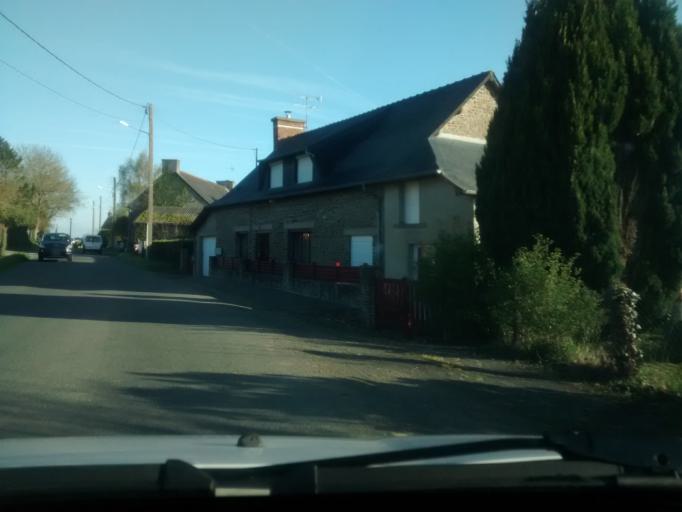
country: FR
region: Brittany
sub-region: Departement d'Ille-et-Vilaine
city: Pleine-Fougeres
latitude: 48.5399
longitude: -1.5689
